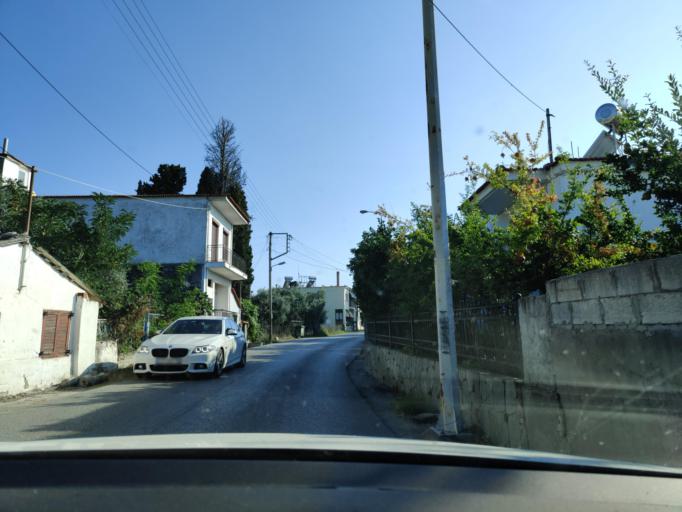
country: GR
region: East Macedonia and Thrace
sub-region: Nomos Kavalas
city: Prinos
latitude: 40.7064
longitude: 24.5333
